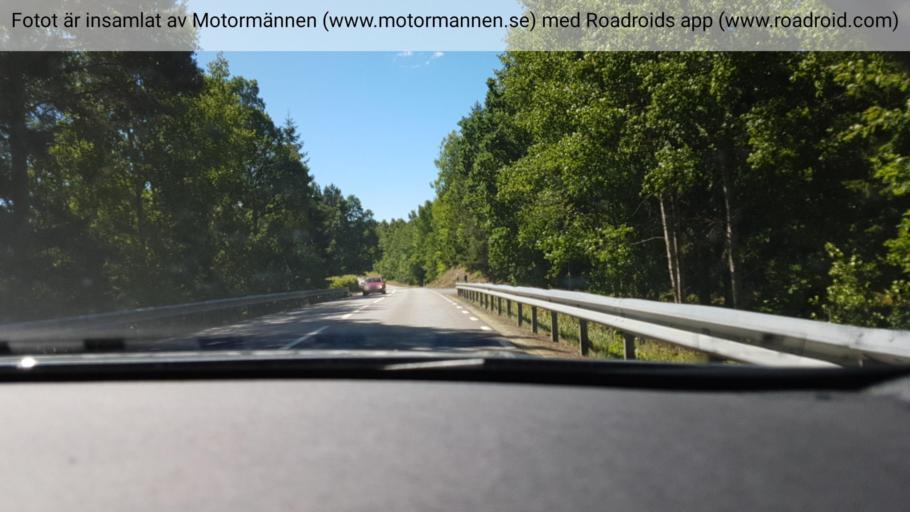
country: SE
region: Joenkoeping
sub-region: Mullsjo Kommun
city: Mullsjoe
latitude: 57.8109
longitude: 13.8512
